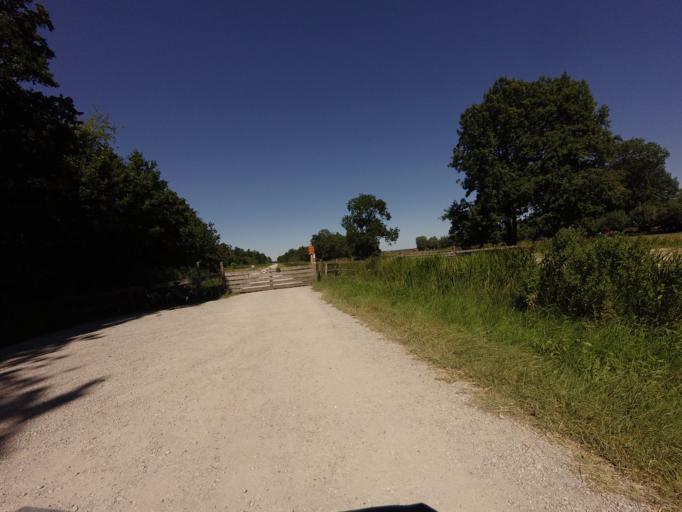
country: NL
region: North Holland
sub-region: Gemeente Wijdemeren
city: Nieuw-Loosdrecht
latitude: 52.1559
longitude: 5.1153
